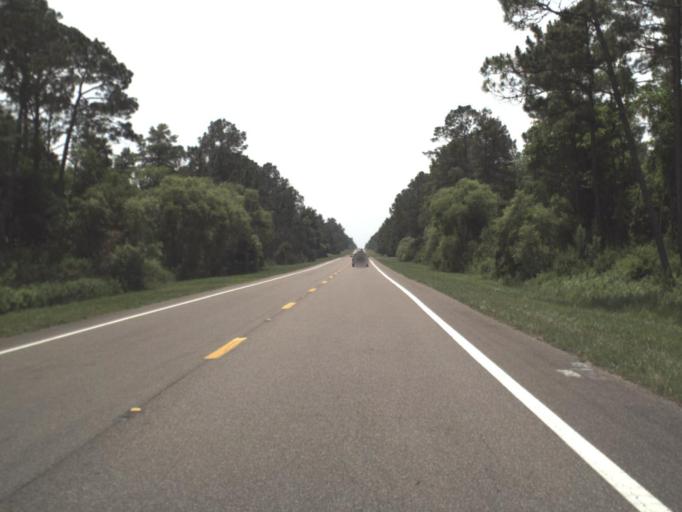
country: US
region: Florida
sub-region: Putnam County
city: Palatka
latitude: 29.4473
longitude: -81.7380
